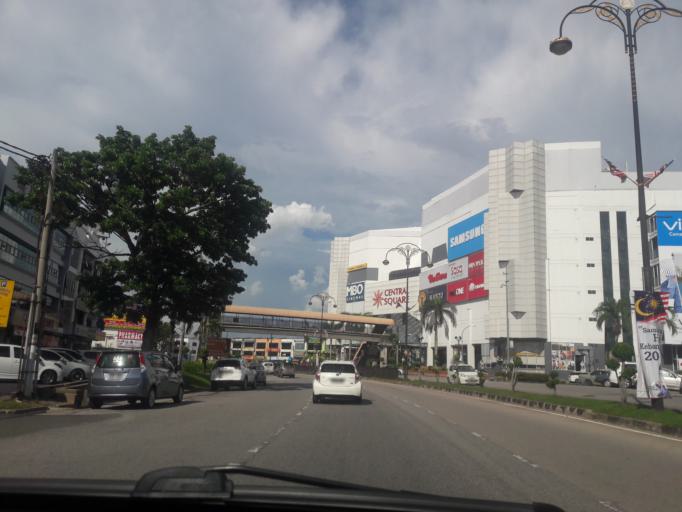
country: MY
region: Kedah
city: Sungai Petani
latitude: 5.6363
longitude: 100.4872
